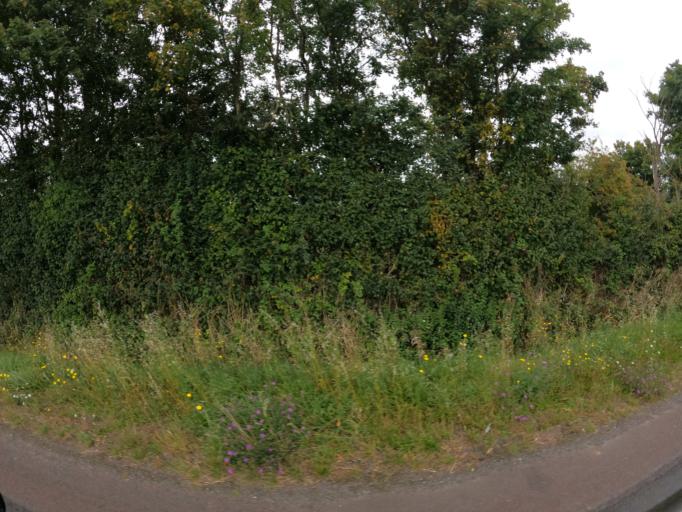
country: FR
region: Pays de la Loire
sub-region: Departement de la Vendee
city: Saint-Michel-le-Cloucq
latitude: 46.4364
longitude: -0.7411
